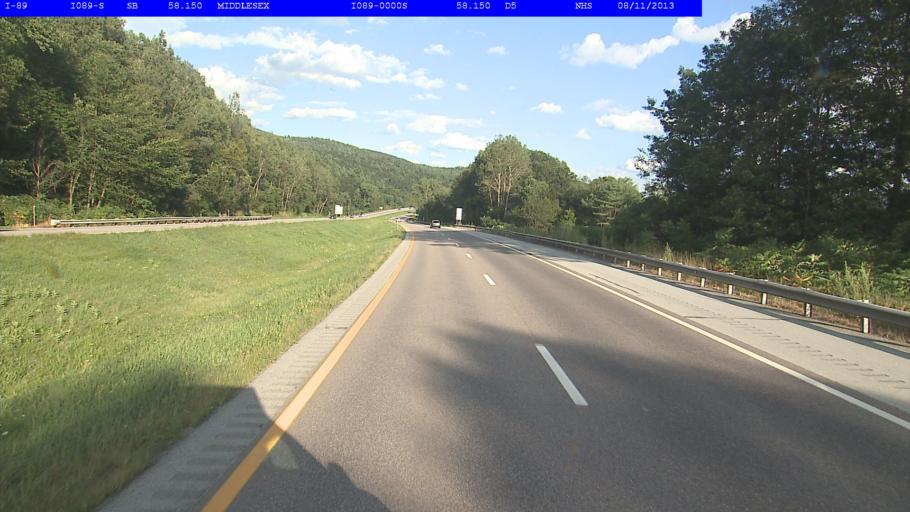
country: US
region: Vermont
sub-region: Washington County
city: Waterbury
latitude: 44.2932
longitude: -72.6762
